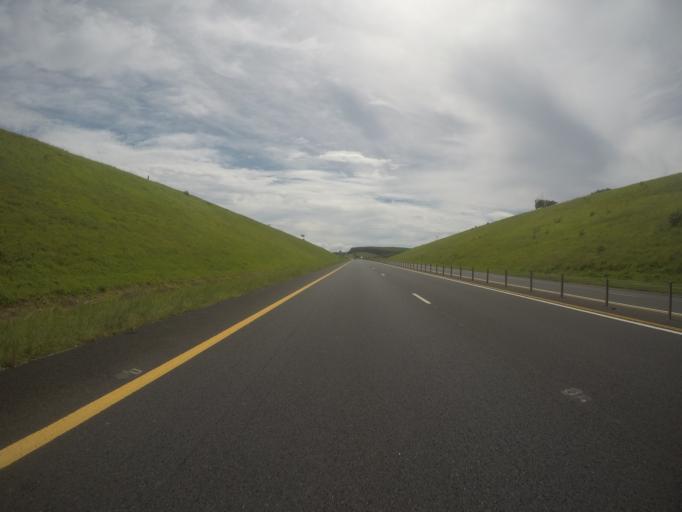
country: ZA
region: KwaZulu-Natal
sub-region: uThungulu District Municipality
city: Eshowe
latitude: -29.0487
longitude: 31.6399
